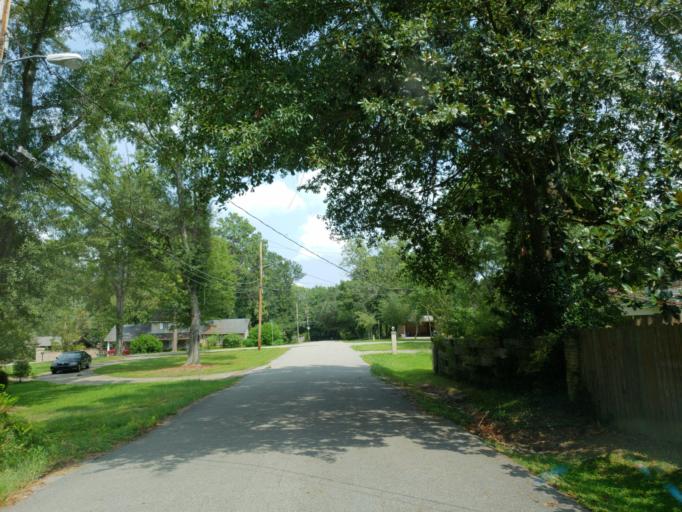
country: US
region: Mississippi
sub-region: Lamar County
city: West Hattiesburg
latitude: 31.3194
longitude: -89.3421
